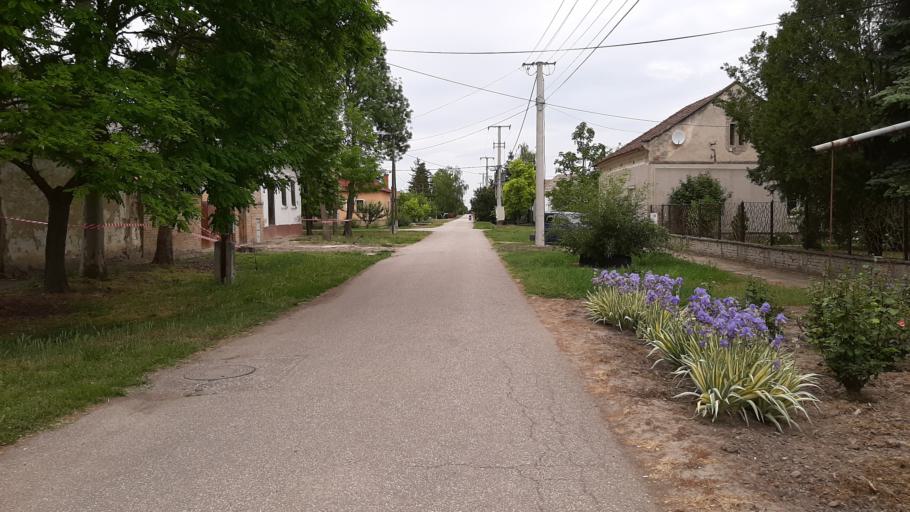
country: RO
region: Timis
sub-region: Comuna Beba Veche
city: Beba Veche
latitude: 46.1485
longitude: 20.2787
